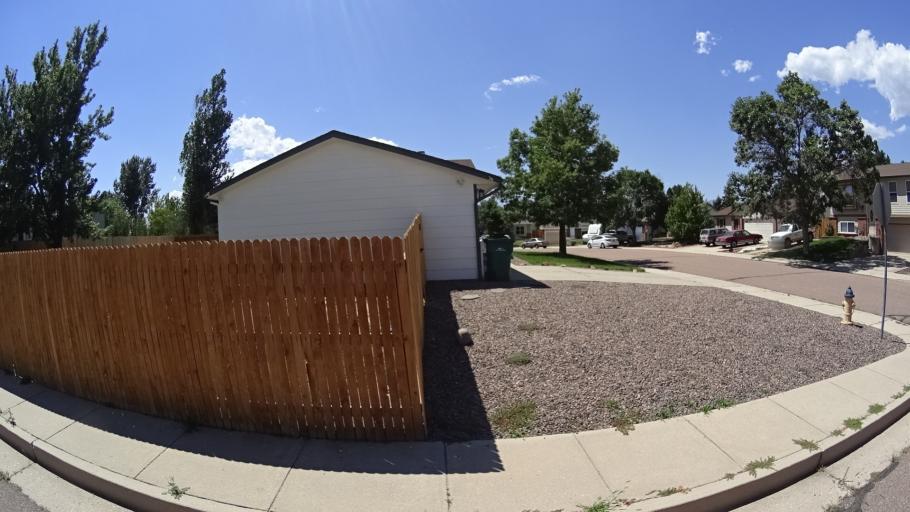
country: US
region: Colorado
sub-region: El Paso County
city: Black Forest
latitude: 38.9501
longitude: -104.7546
